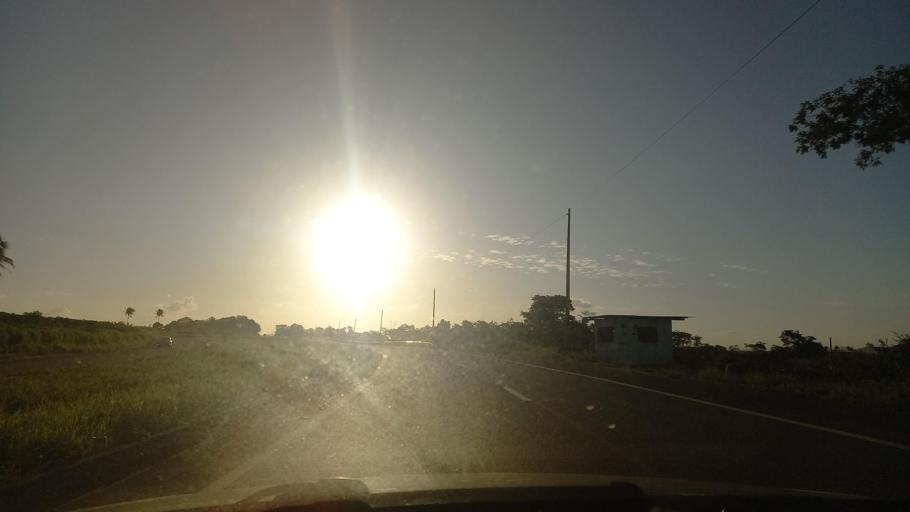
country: BR
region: Alagoas
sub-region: Limoeiro De Anadia
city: Limoeiro de Anadia
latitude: -9.7584
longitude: -36.5152
